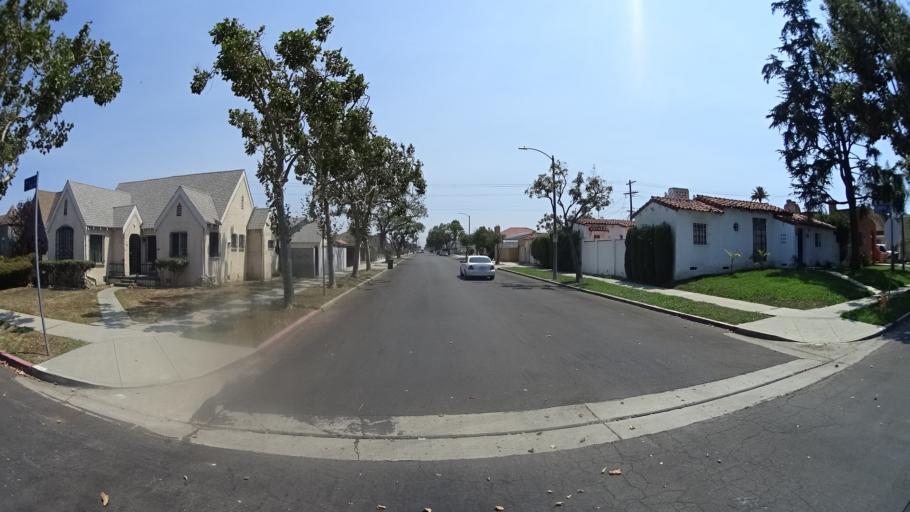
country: US
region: California
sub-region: Los Angeles County
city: Westmont
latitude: 33.9699
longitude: -118.3134
